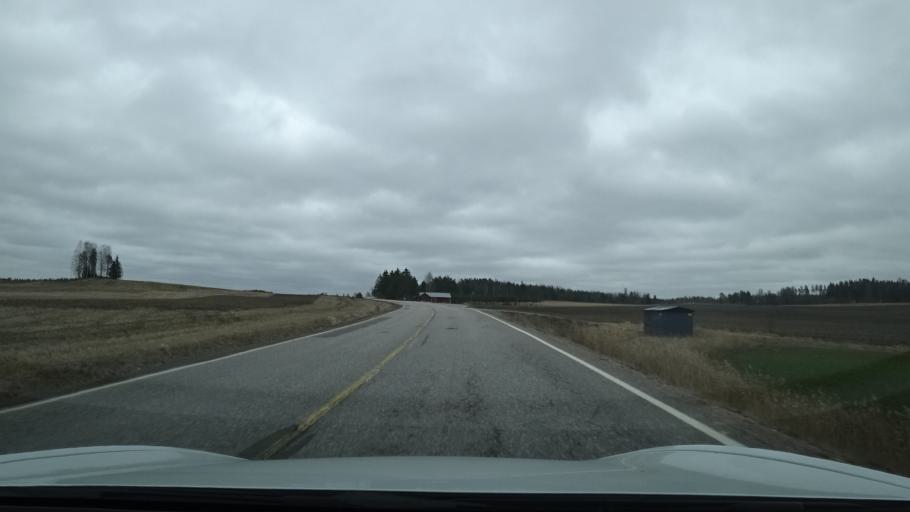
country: FI
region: Uusimaa
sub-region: Porvoo
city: Myrskylae
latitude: 60.6593
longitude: 25.8110
